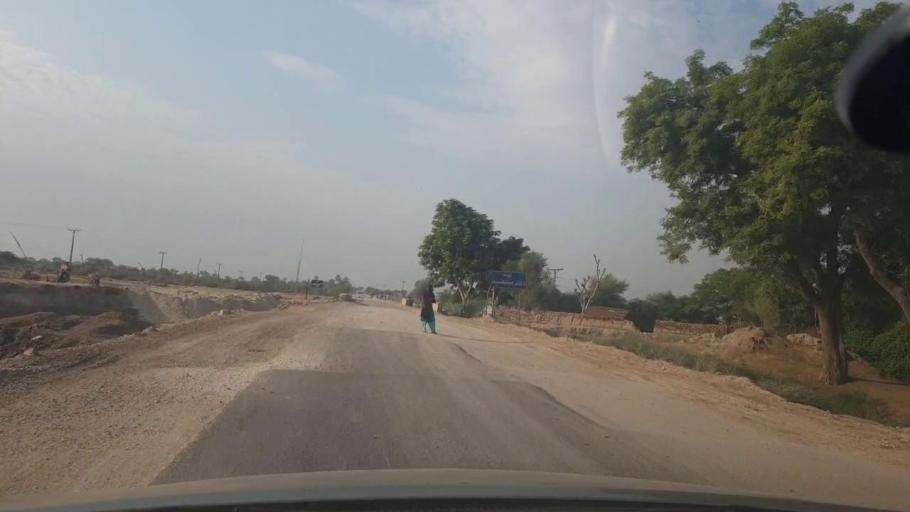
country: PK
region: Sindh
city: Jacobabad
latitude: 28.1987
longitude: 68.3678
